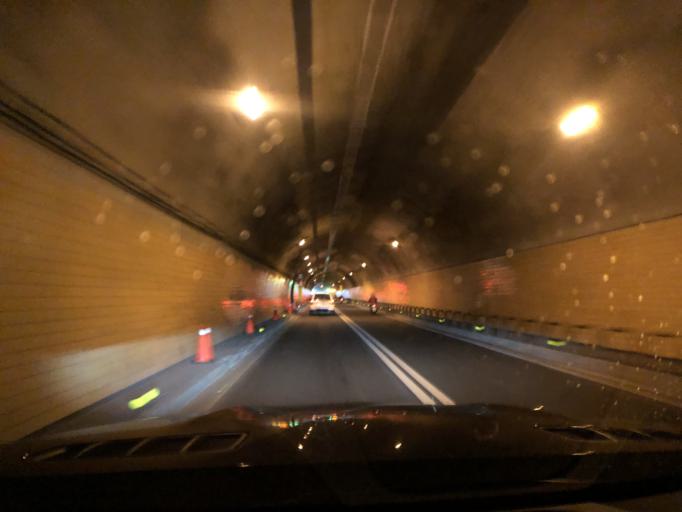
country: TW
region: Taipei
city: Taipei
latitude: 24.9936
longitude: 121.5515
